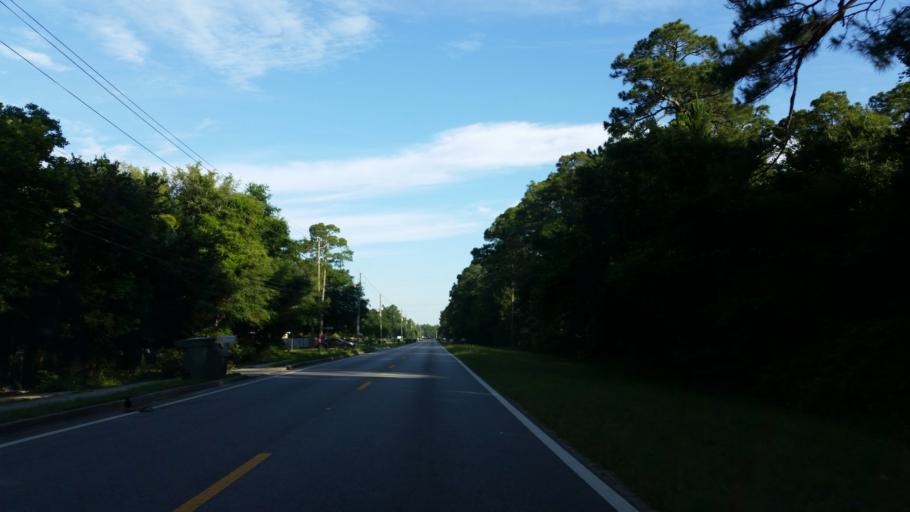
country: US
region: Florida
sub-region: Escambia County
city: Myrtle Grove
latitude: 30.3927
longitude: -87.3649
